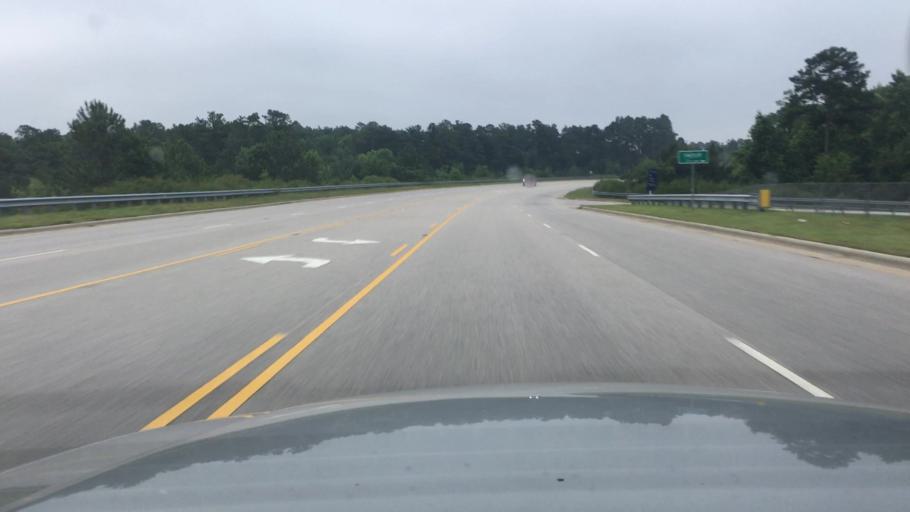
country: US
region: North Carolina
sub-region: Cumberland County
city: Fayetteville
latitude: 35.0169
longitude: -78.8900
